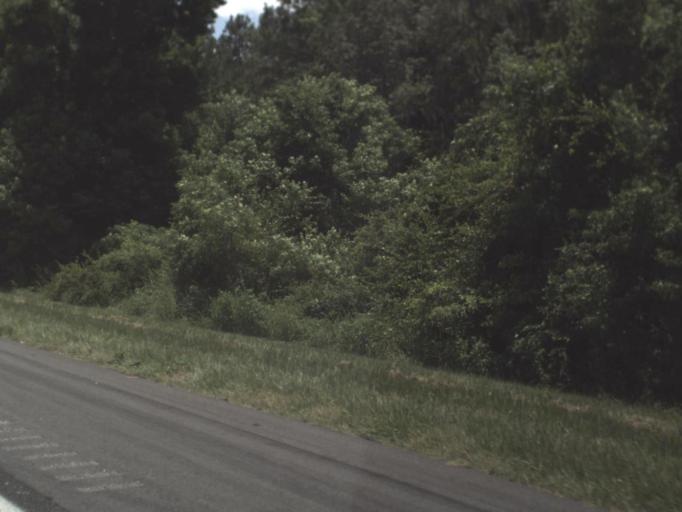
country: US
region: Florida
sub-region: Madison County
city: Madison
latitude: 30.4344
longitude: -83.5307
